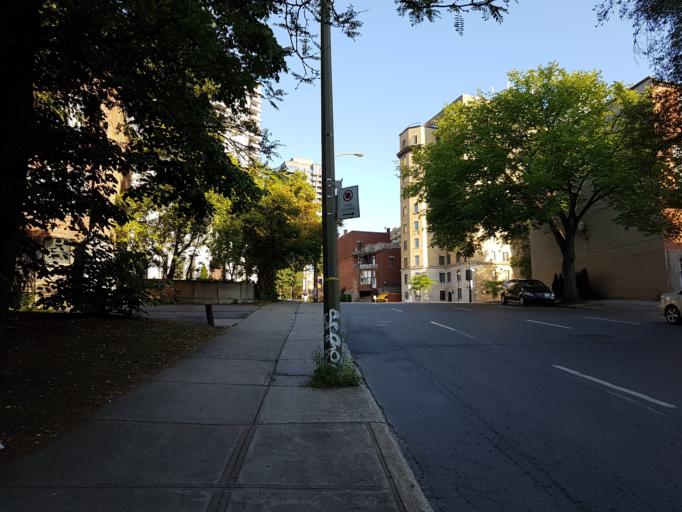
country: CA
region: Quebec
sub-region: Montreal
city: Montreal
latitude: 45.4959
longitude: -73.5828
